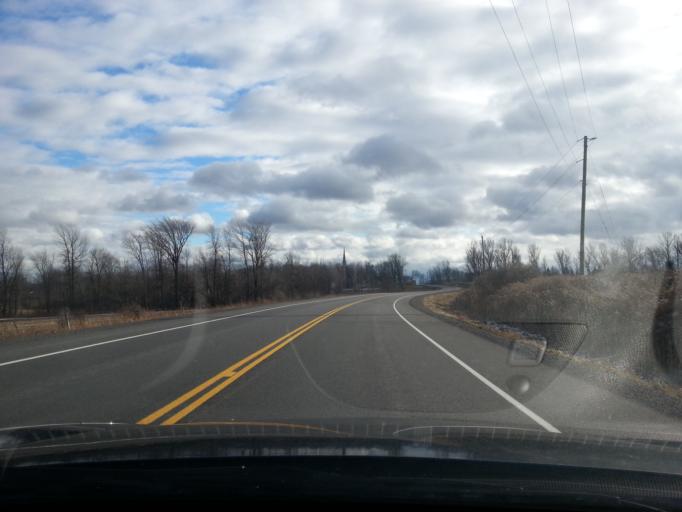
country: CA
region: Ontario
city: Prescott
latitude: 45.0554
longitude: -75.5118
